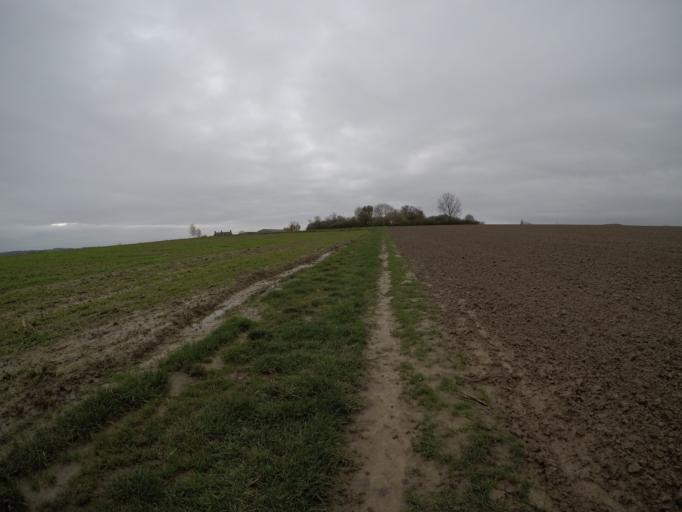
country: BE
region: Flanders
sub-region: Provincie West-Vlaanderen
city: Saint-Yvon
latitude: 50.7774
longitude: 2.8647
